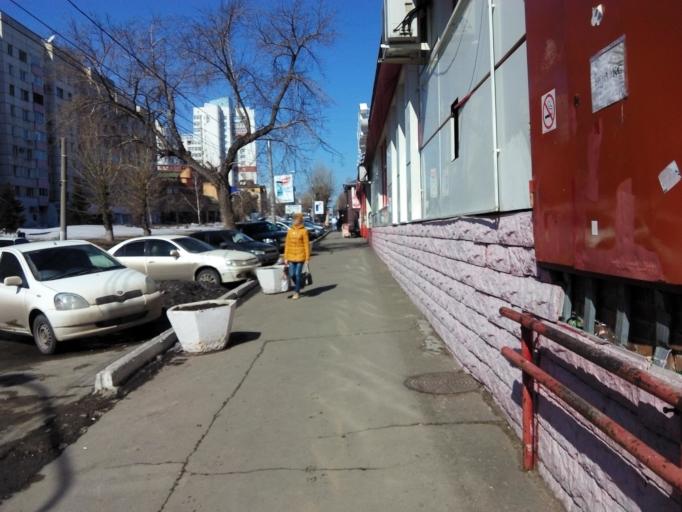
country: RU
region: Altai Krai
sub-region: Gorod Barnaulskiy
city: Barnaul
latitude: 53.3407
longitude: 83.7792
